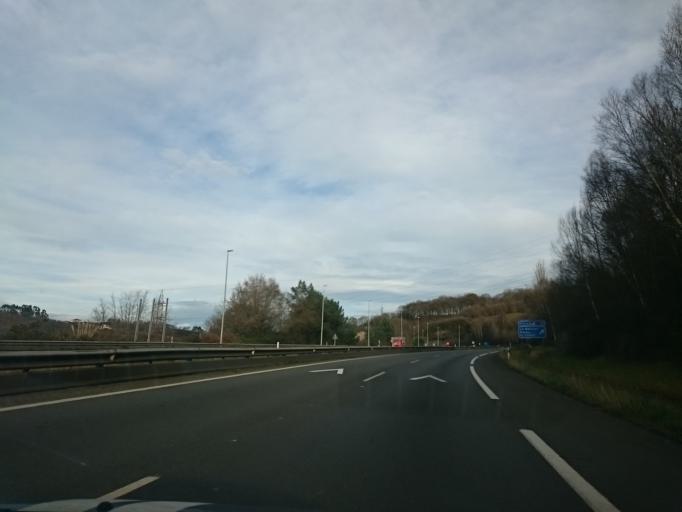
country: ES
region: Asturias
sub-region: Province of Asturias
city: Castandiello
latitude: 43.3207
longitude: -5.8701
